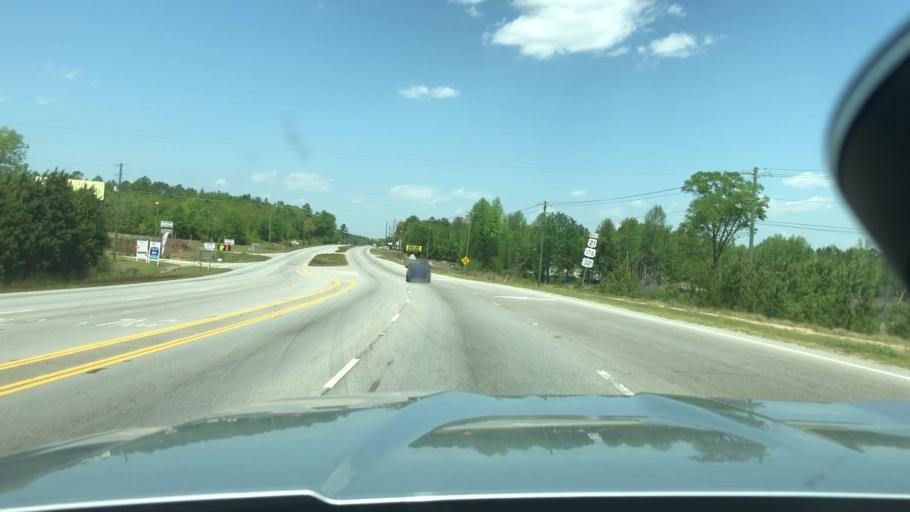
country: US
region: South Carolina
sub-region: Lexington County
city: Pineridge
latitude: 33.8951
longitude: -81.0620
